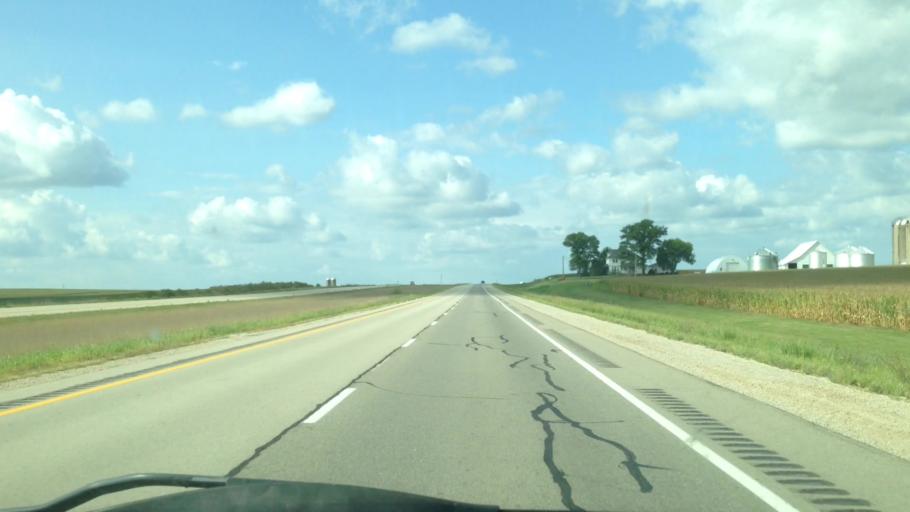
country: US
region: Iowa
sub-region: Henry County
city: Mount Pleasant
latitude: 40.7882
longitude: -91.5641
